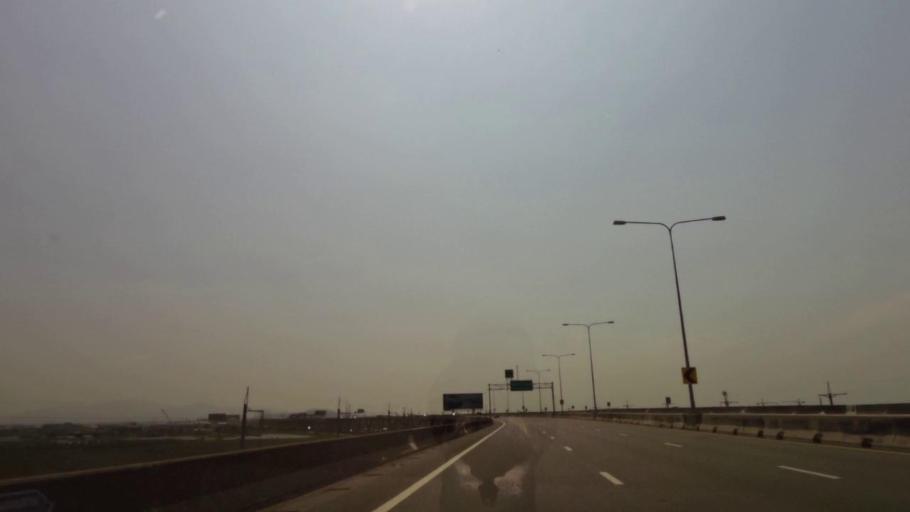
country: TH
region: Chachoengsao
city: Bang Pakong
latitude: 13.4667
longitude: 100.9965
